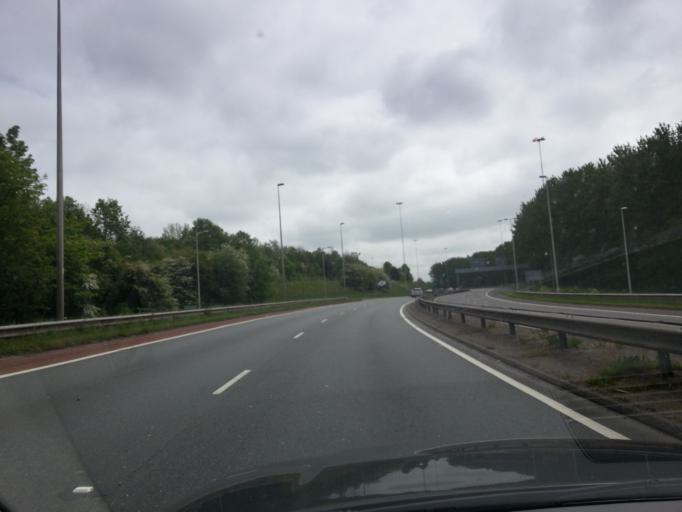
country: GB
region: England
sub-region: Cheshire West and Chester
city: Frodsham
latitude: 53.3179
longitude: -2.7319
